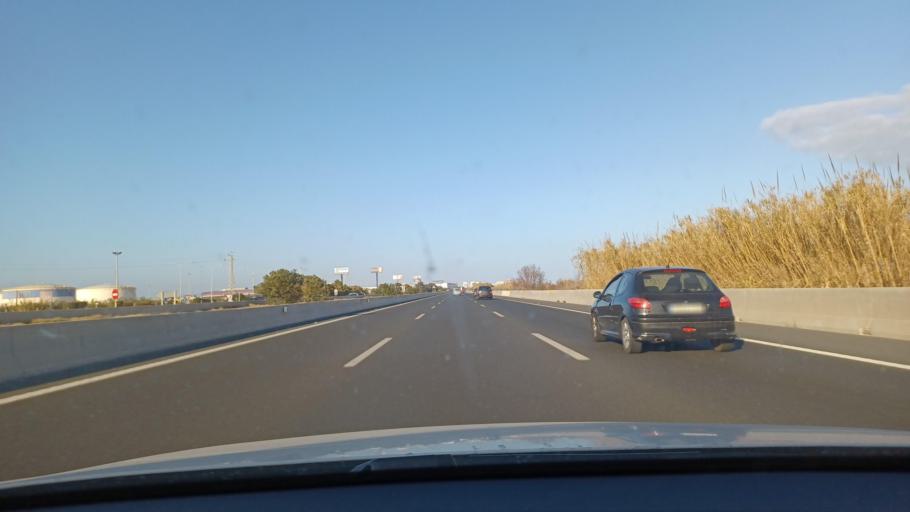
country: ES
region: Valencia
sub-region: Provincia de Valencia
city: Albuixech
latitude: 39.5299
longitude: -0.3120
